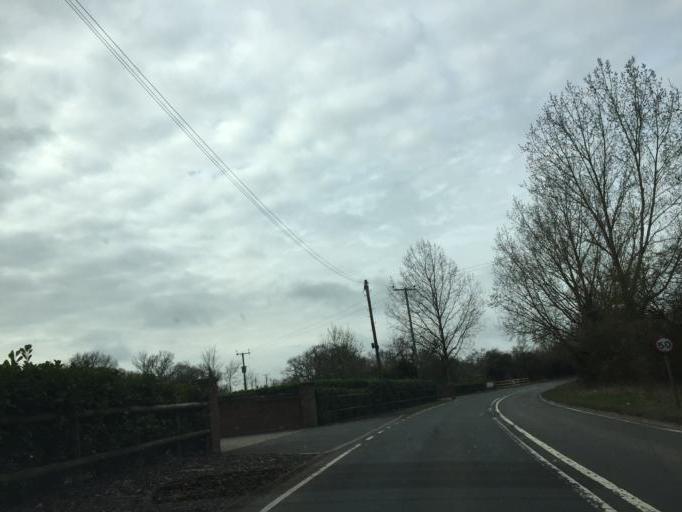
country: GB
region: England
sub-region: Warwickshire
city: Studley
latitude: 52.2989
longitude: -1.8416
